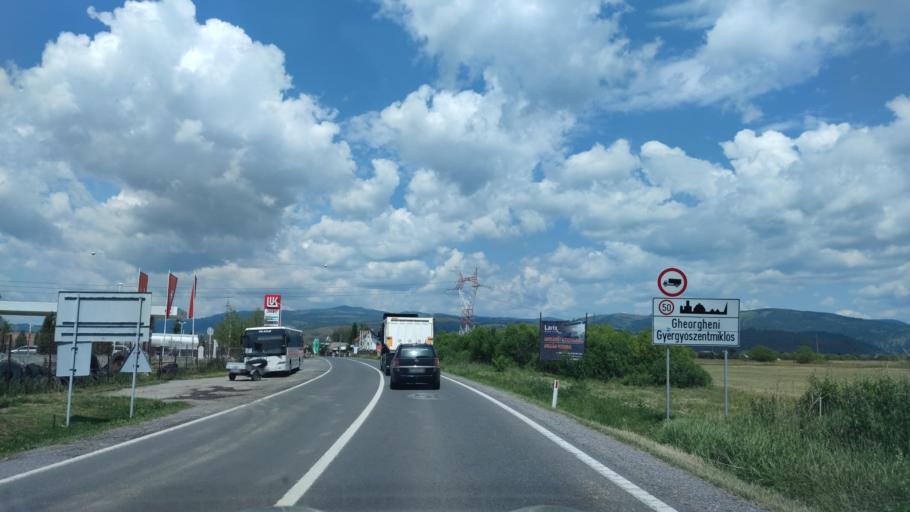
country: RO
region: Harghita
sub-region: Municipiul Gheorgheni
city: Gheorgheni
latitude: 46.7113
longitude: 25.6020
